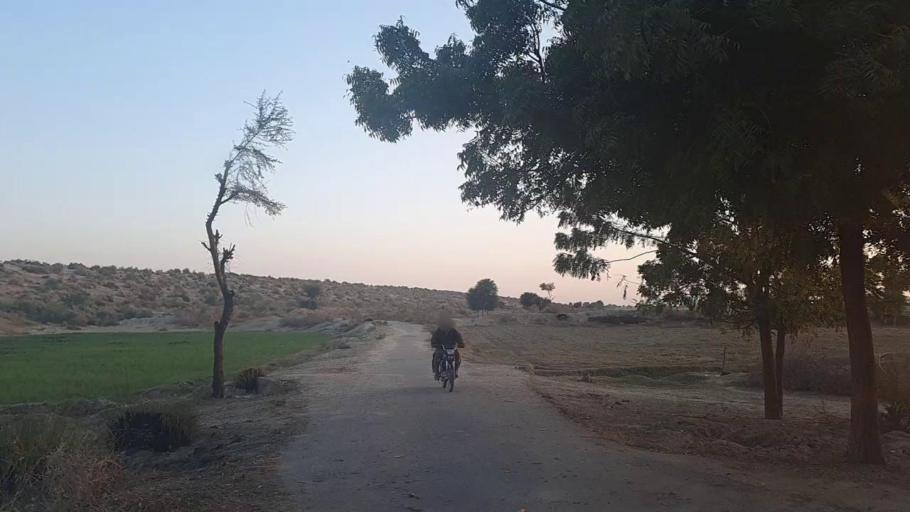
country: PK
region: Sindh
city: Jam Sahib
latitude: 26.3847
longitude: 68.6902
